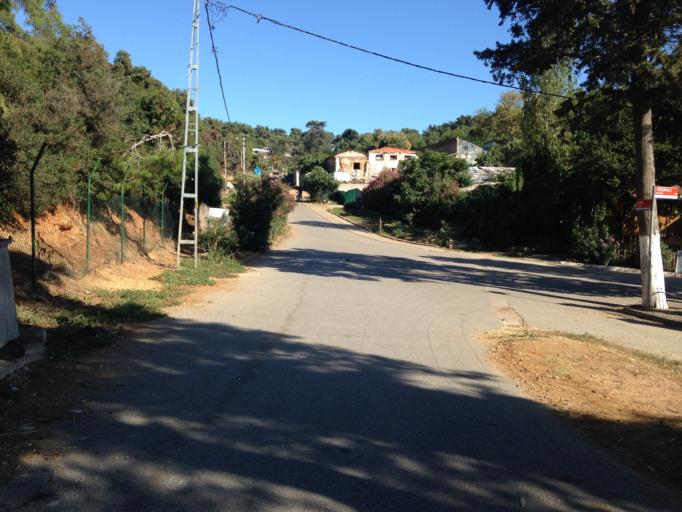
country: TR
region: Istanbul
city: Adalar
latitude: 40.8598
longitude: 29.1152
